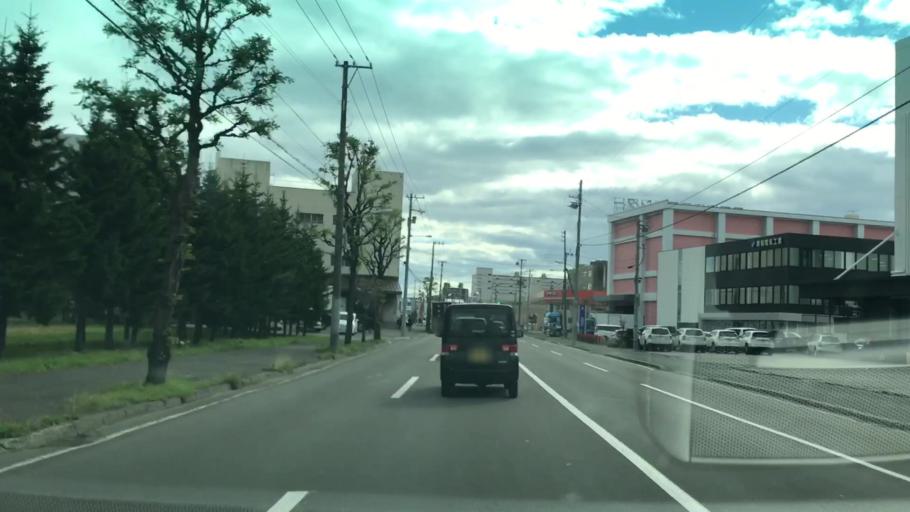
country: JP
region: Hokkaido
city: Sapporo
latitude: 43.0737
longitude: 141.3169
